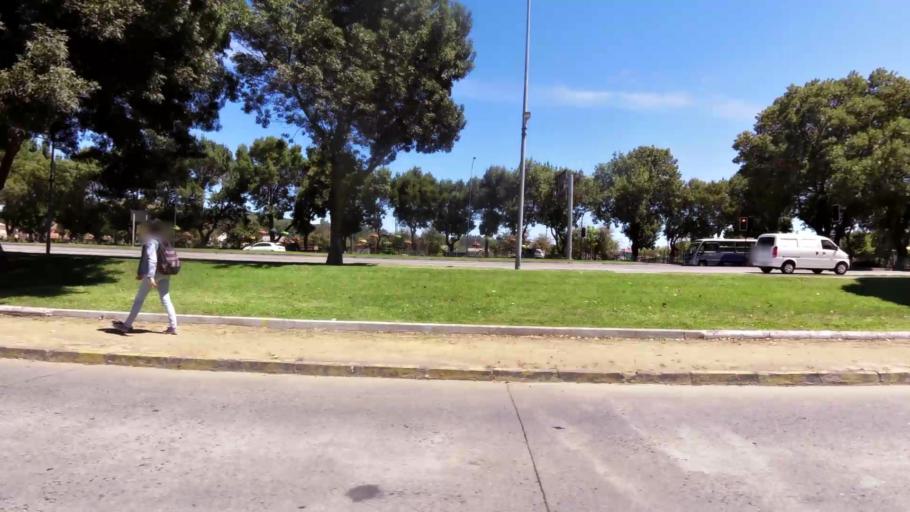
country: CL
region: Biobio
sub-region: Provincia de Concepcion
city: Talcahuano
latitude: -36.7623
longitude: -73.0877
